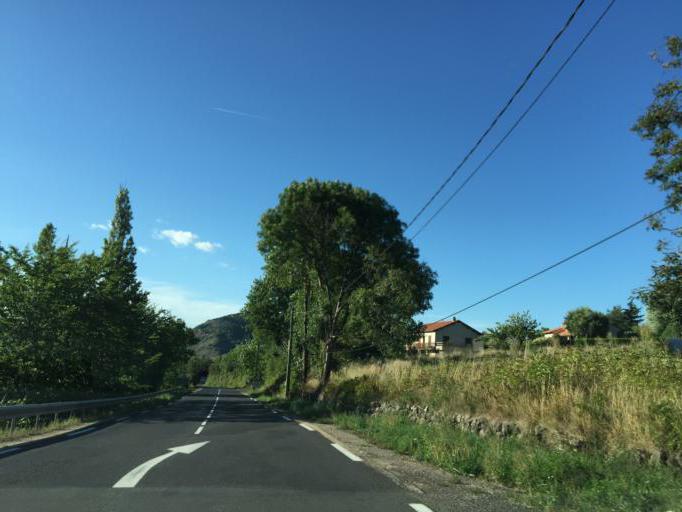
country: FR
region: Auvergne
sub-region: Departement de la Haute-Loire
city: Espaly-Saint-Marcel
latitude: 45.0391
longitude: 3.8648
